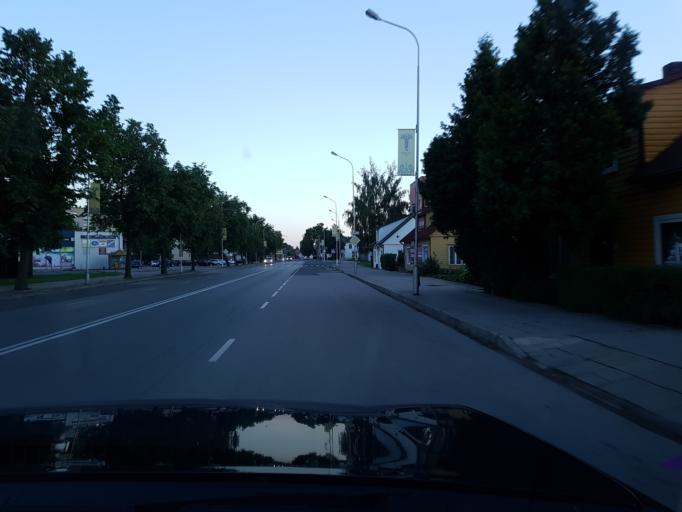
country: LT
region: Marijampoles apskritis
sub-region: Marijampole Municipality
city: Marijampole
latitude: 54.5645
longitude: 23.3560
